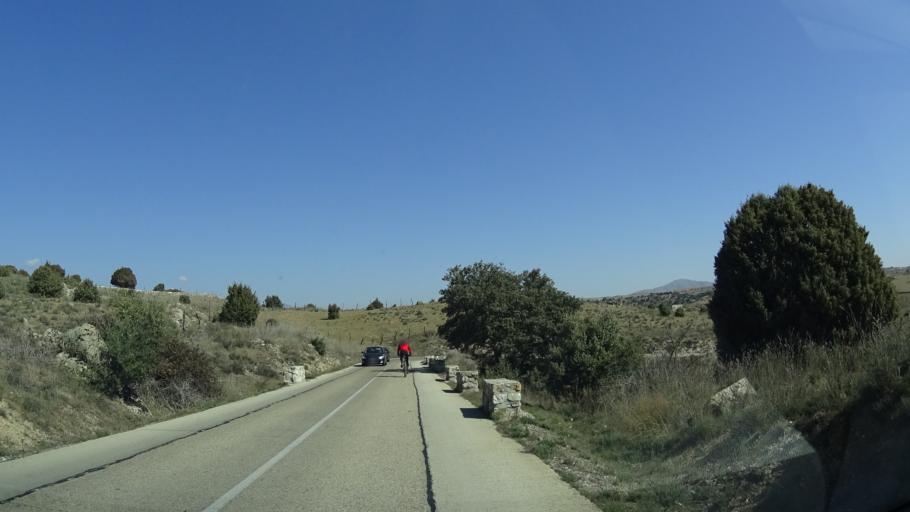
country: ES
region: Madrid
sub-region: Provincia de Madrid
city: Colmenar Viejo
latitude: 40.6450
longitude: -3.8110
